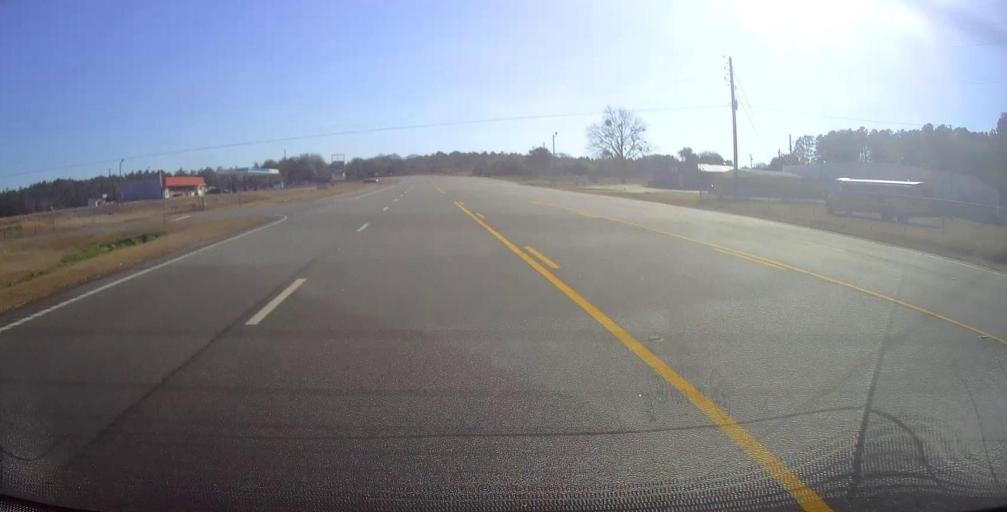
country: US
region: Georgia
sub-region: Taylor County
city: Butler
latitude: 32.5763
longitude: -84.2389
